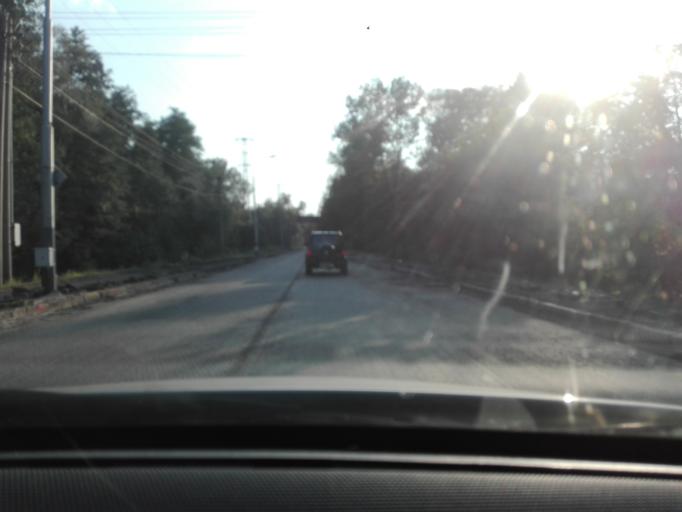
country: CZ
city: Rychvald
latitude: 49.8428
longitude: 18.3518
